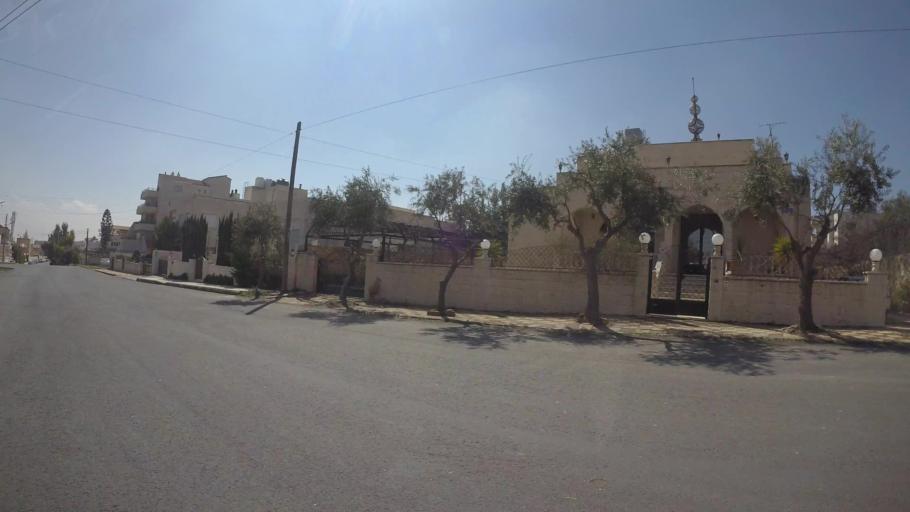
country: JO
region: Amman
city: Al Bunayyat ash Shamaliyah
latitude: 31.8978
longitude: 35.8860
